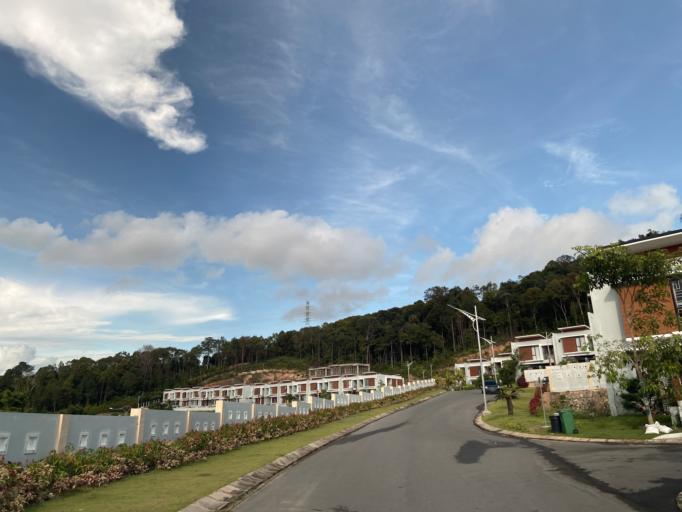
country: SG
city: Singapore
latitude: 1.0940
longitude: 104.0282
